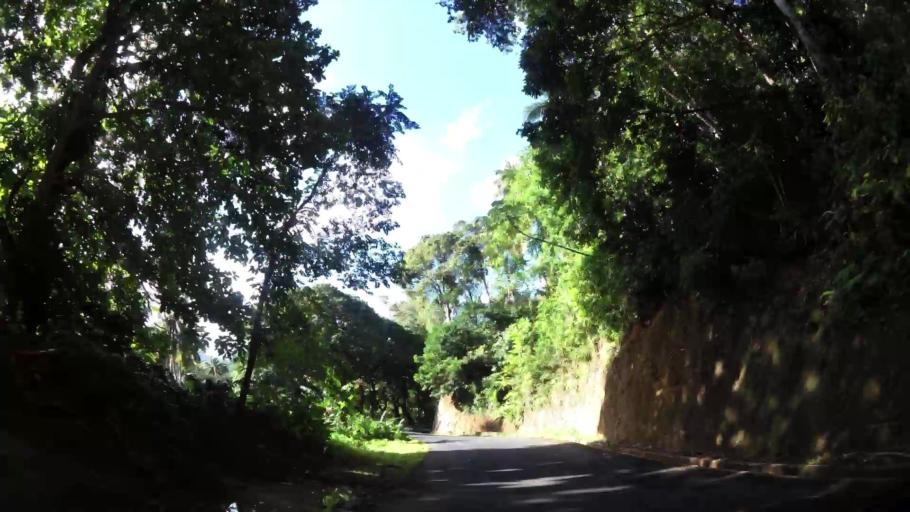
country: DM
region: Saint Andrew
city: Calibishie
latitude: 15.5890
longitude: -61.3994
